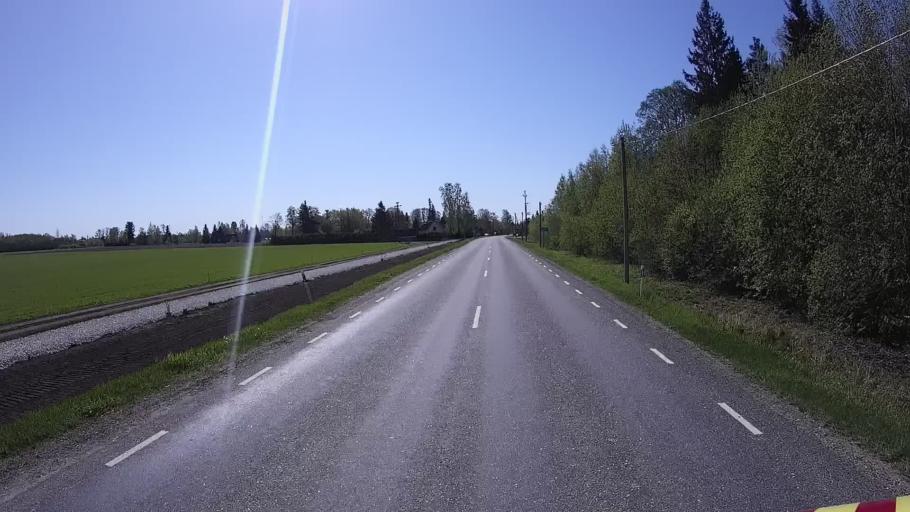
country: EE
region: Paernumaa
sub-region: Tootsi vald
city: Tootsi
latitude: 58.4913
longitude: 24.8087
